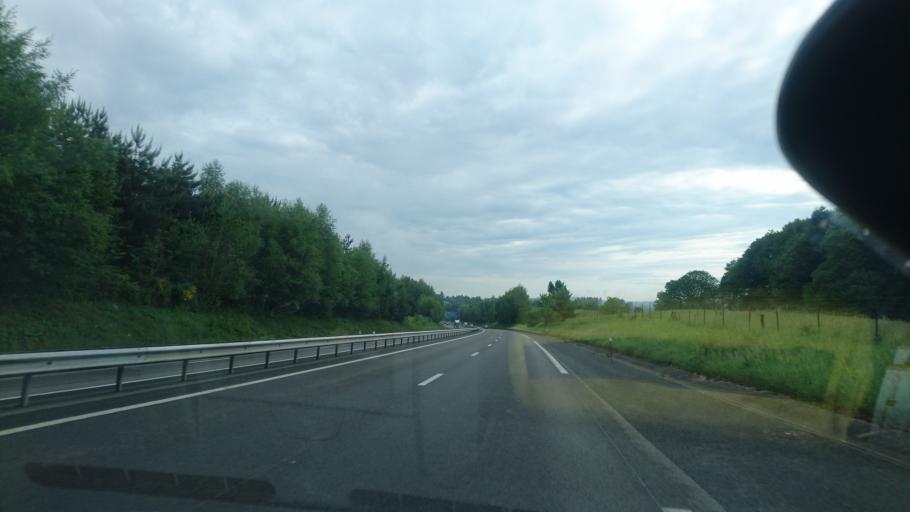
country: FR
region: Limousin
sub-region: Departement de la Correze
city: Sainte-Fereole
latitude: 45.2898
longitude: 1.5733
